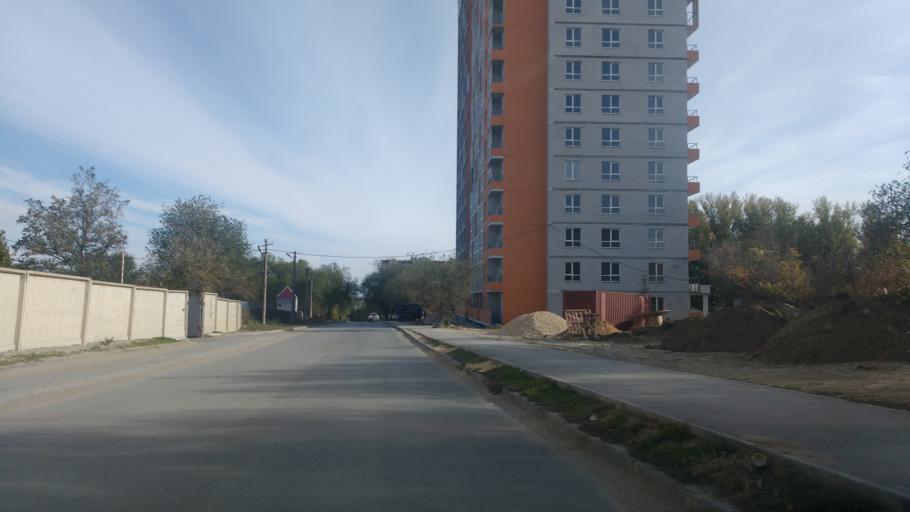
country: RU
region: Volgograd
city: Krasnoslobodsk
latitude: 48.7647
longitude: 44.5496
